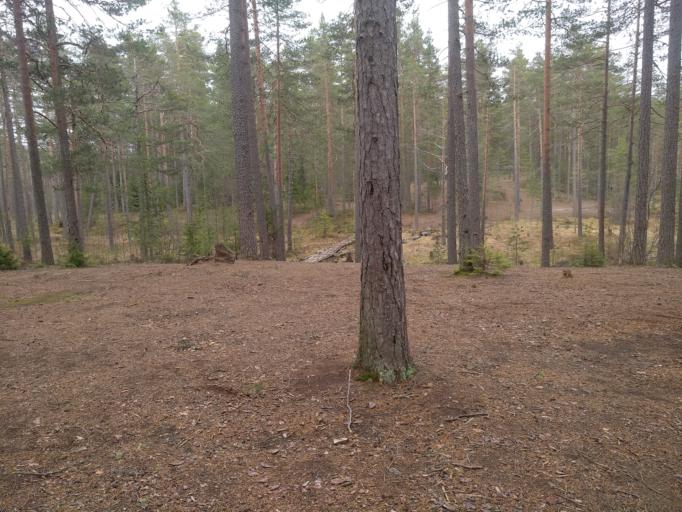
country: RU
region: Leningrad
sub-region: Vsevolzhskij Rajon
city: Vaskelovo
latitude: 60.4506
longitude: 30.3209
